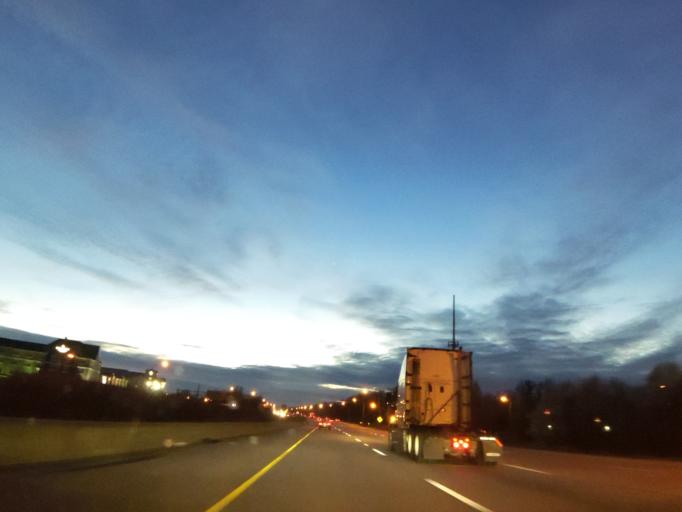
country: US
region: Kentucky
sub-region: Jefferson County
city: Douglass Hills
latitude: 38.2239
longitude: -85.5401
